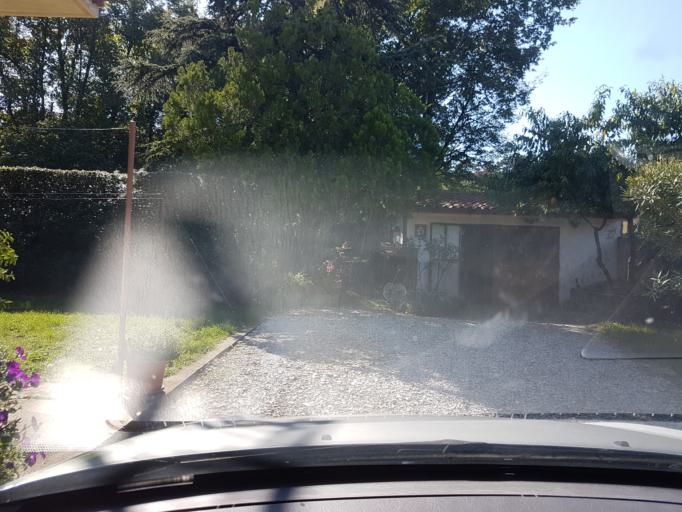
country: IT
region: Friuli Venezia Giulia
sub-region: Provincia di Trieste
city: Aurisina
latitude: 45.7479
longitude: 13.6737
